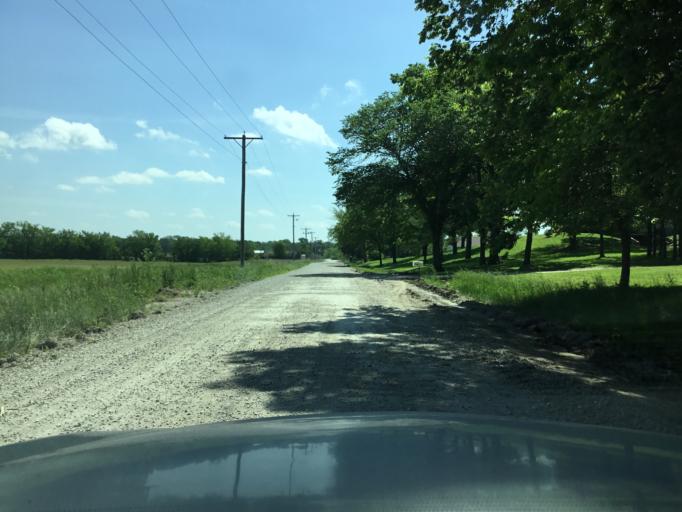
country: US
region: Kansas
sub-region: Labette County
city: Parsons
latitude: 37.3110
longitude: -95.2537
